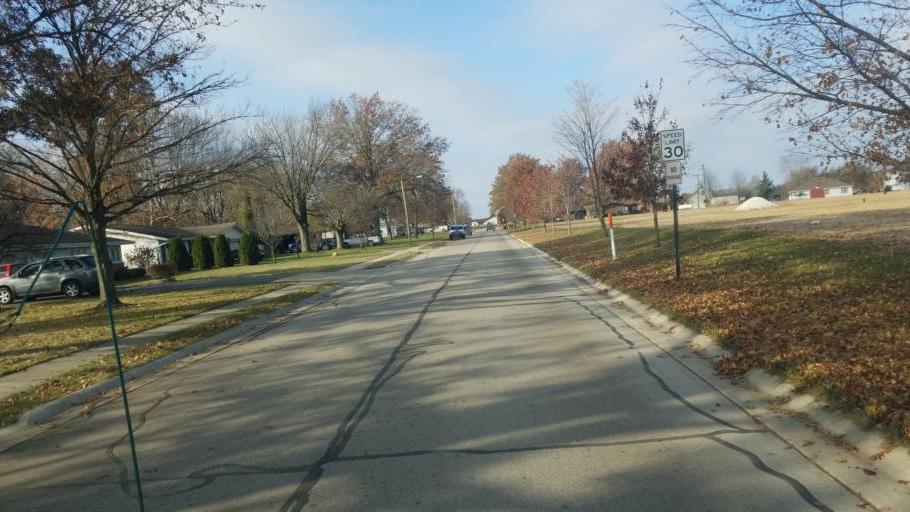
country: US
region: Indiana
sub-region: Adams County
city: Berne
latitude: 40.6594
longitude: -84.9607
